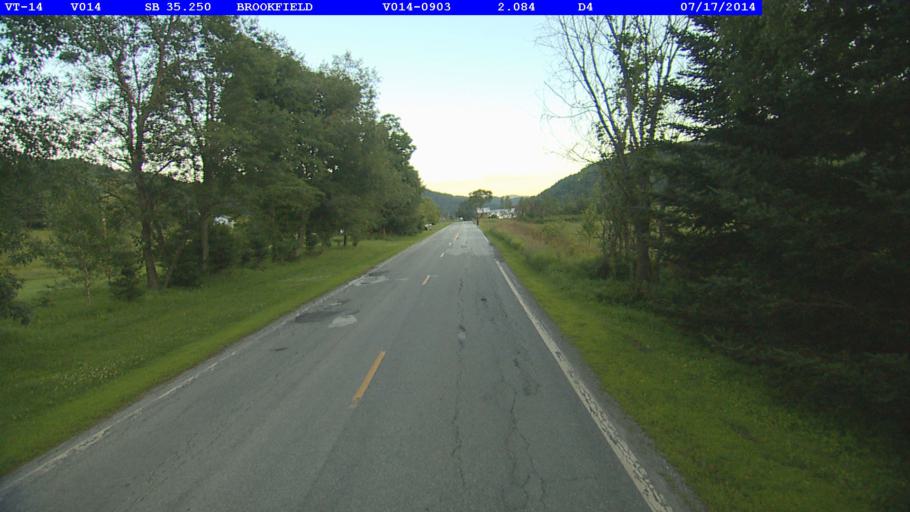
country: US
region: Vermont
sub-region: Orange County
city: Williamstown
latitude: 44.0074
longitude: -72.5655
